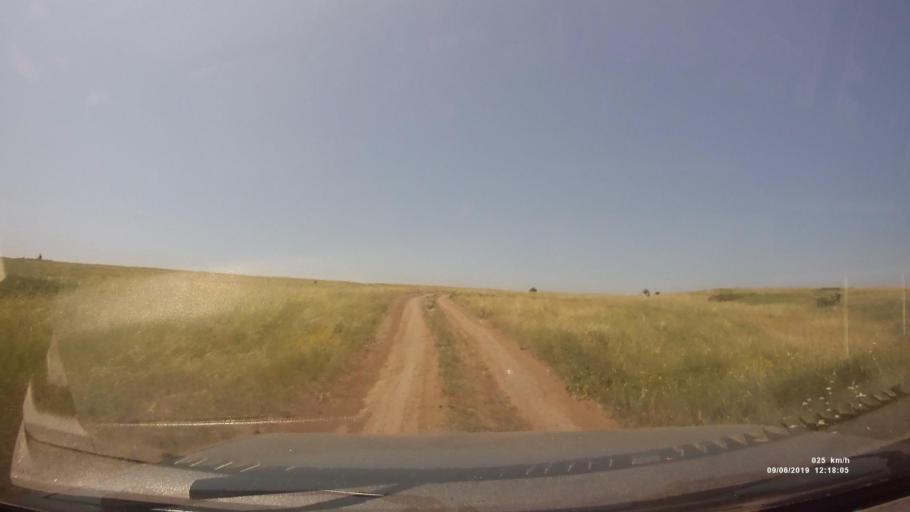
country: RU
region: Rostov
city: Kamensk-Shakhtinskiy
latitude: 48.2556
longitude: 40.3111
